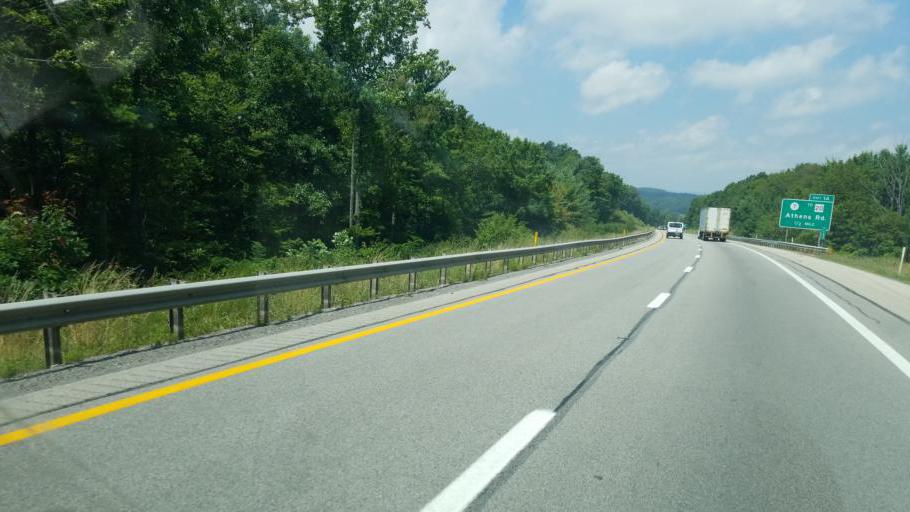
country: US
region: West Virginia
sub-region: Mercer County
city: Athens
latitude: 37.4135
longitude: -81.0620
